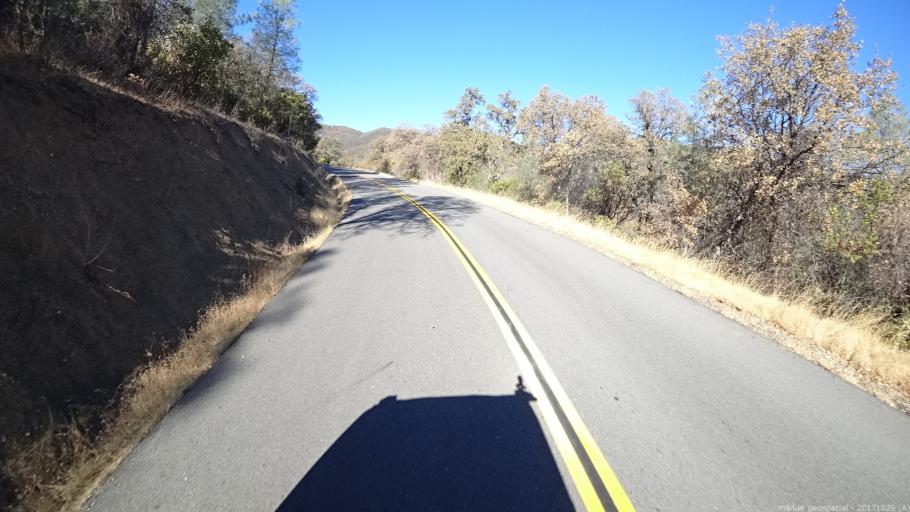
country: US
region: California
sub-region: Trinity County
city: Lewiston
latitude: 40.3891
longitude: -122.8173
